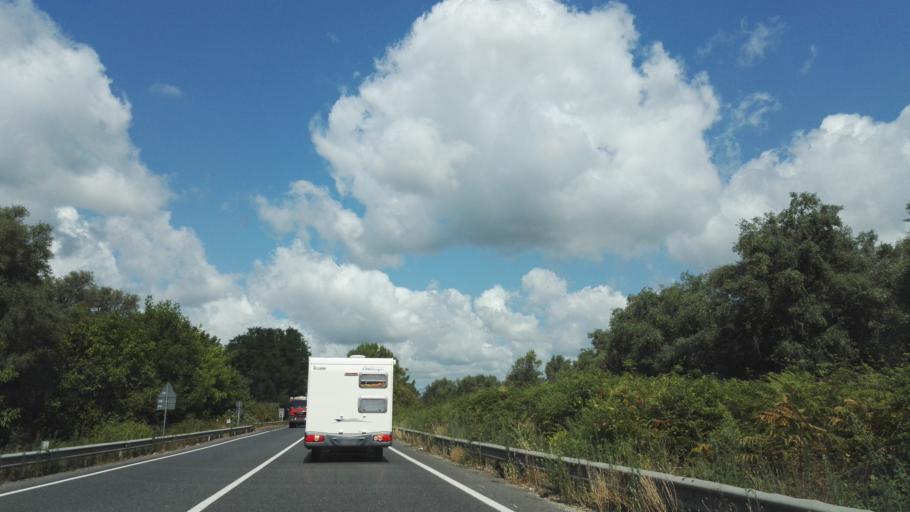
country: IT
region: Calabria
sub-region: Provincia di Reggio Calabria
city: Melicucco
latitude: 38.4268
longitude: 16.0581
